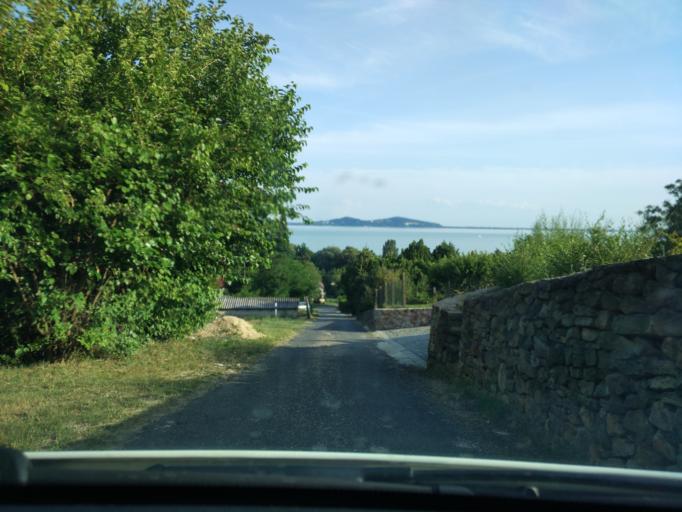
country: HU
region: Veszprem
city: Badacsonytomaj
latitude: 46.8077
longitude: 17.5431
